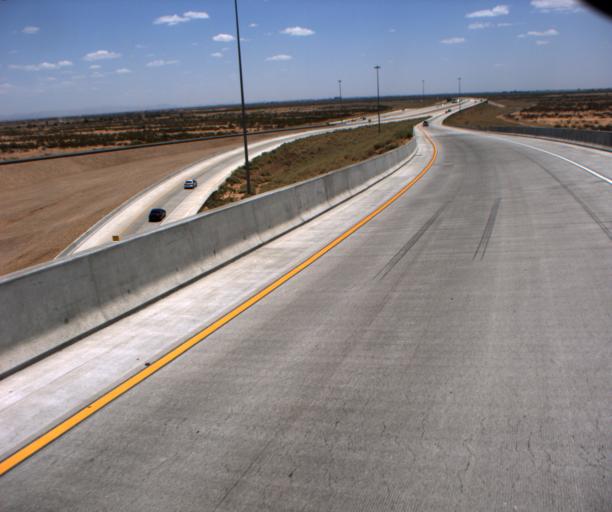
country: US
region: Arizona
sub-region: Maricopa County
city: Queen Creek
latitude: 33.3294
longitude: -111.6503
